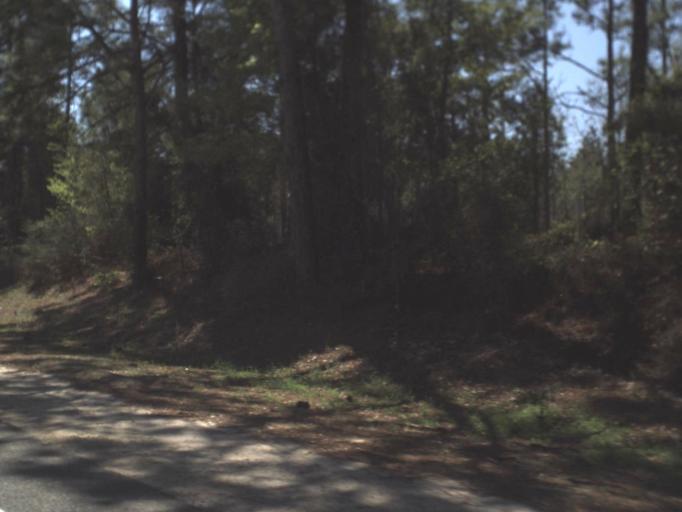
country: US
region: Florida
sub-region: Leon County
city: Woodville
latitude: 30.3524
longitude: -84.2600
